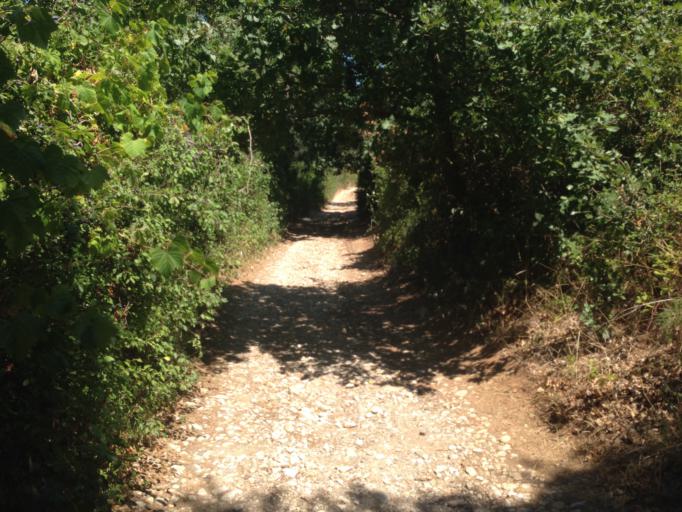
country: HR
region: Istarska
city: Medulin
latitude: 44.7856
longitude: 13.9099
